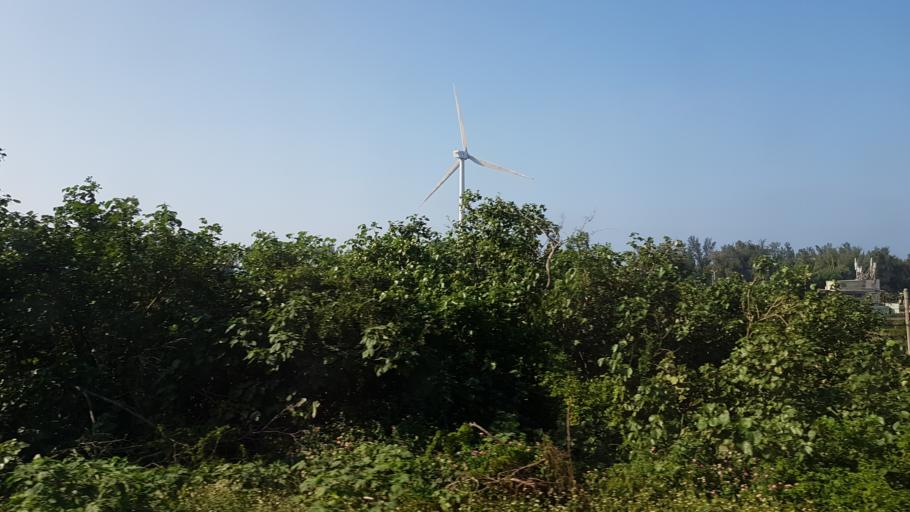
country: TW
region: Taiwan
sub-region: Hsinchu
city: Hsinchu
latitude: 24.7323
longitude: 120.8824
